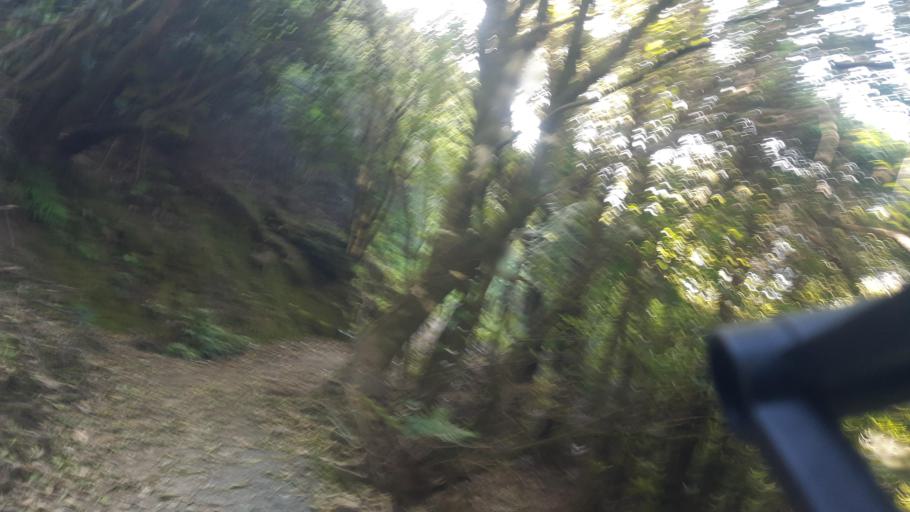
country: NZ
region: Marlborough
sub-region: Marlborough District
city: Picton
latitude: -41.2787
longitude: 173.7847
